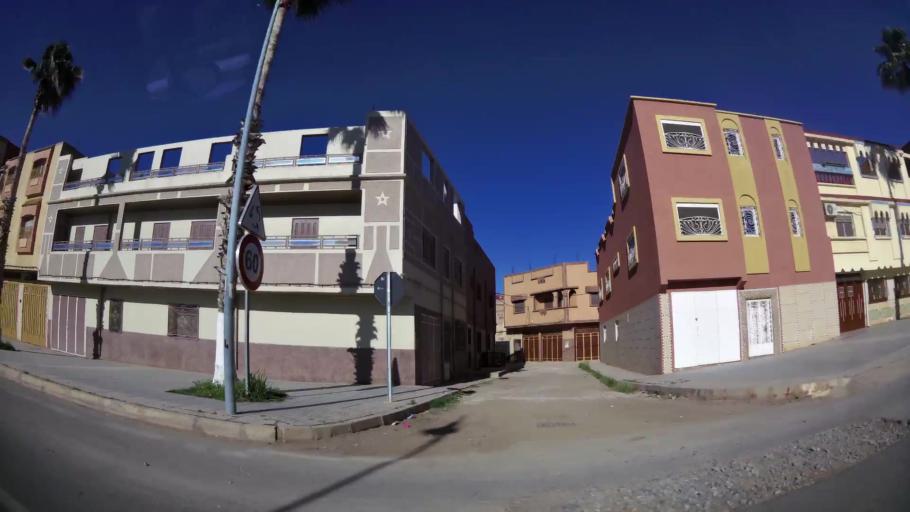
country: MA
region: Oriental
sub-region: Berkane-Taourirt
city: Ahfir
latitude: 34.9576
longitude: -2.1069
